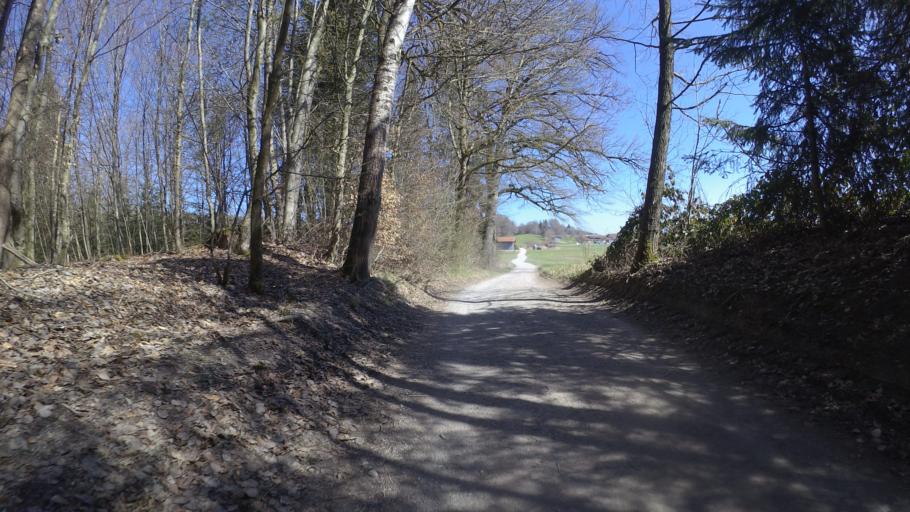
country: DE
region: Bavaria
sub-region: Upper Bavaria
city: Chieming
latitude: 47.9236
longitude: 12.5206
